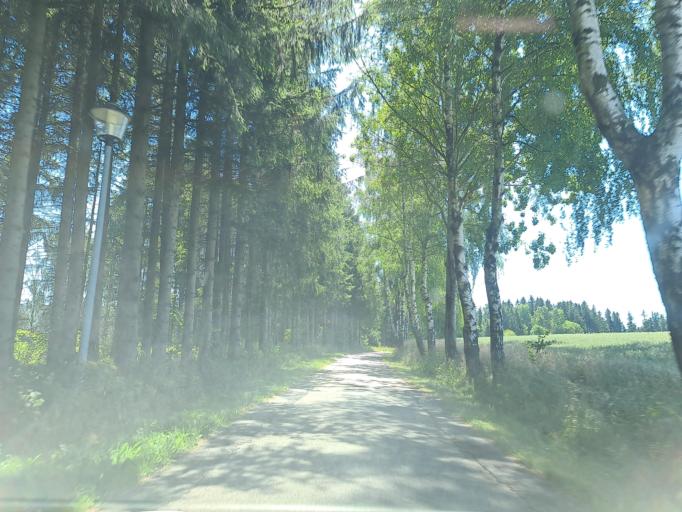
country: DE
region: Saxony
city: Neuhausen
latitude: 50.6970
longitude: 13.4999
